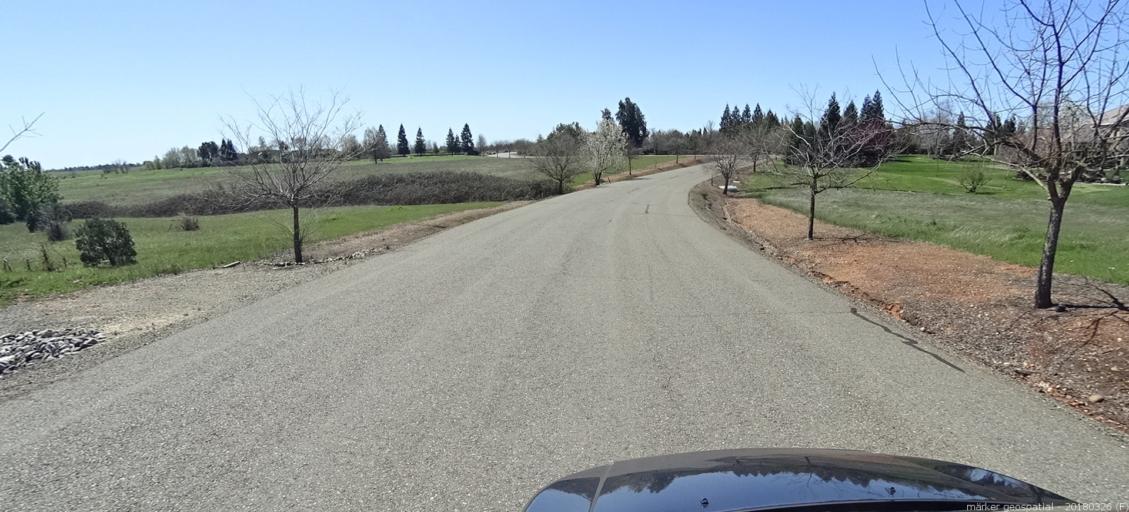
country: US
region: California
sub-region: Sacramento County
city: Vineyard
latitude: 38.4865
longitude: -121.2906
